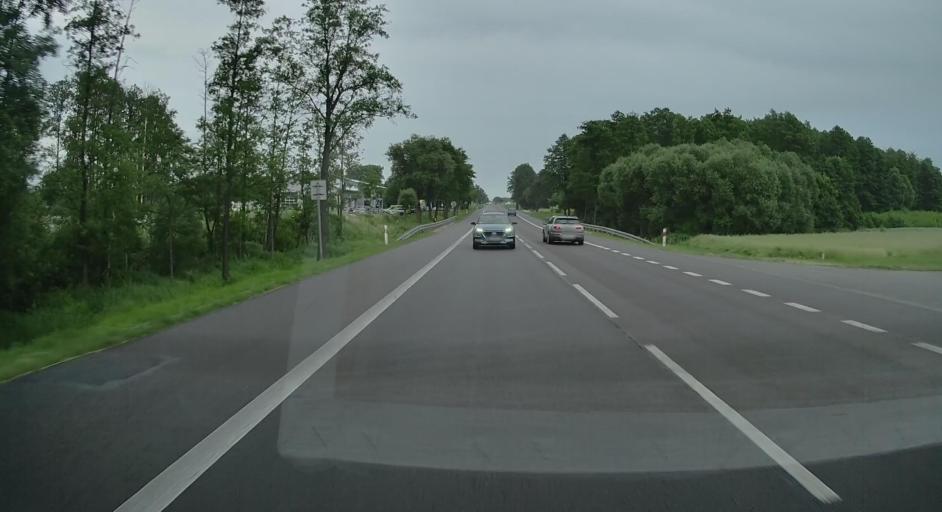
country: PL
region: Lublin Voivodeship
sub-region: Powiat bialski
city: Miedzyrzec Podlaski
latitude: 52.0015
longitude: 22.8183
